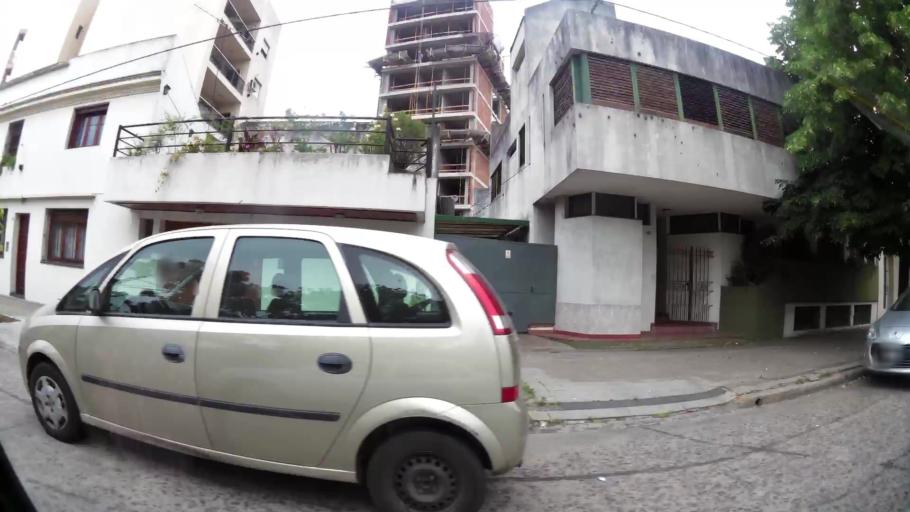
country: AR
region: Buenos Aires
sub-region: Partido de La Plata
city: La Plata
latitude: -34.9222
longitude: -57.9667
